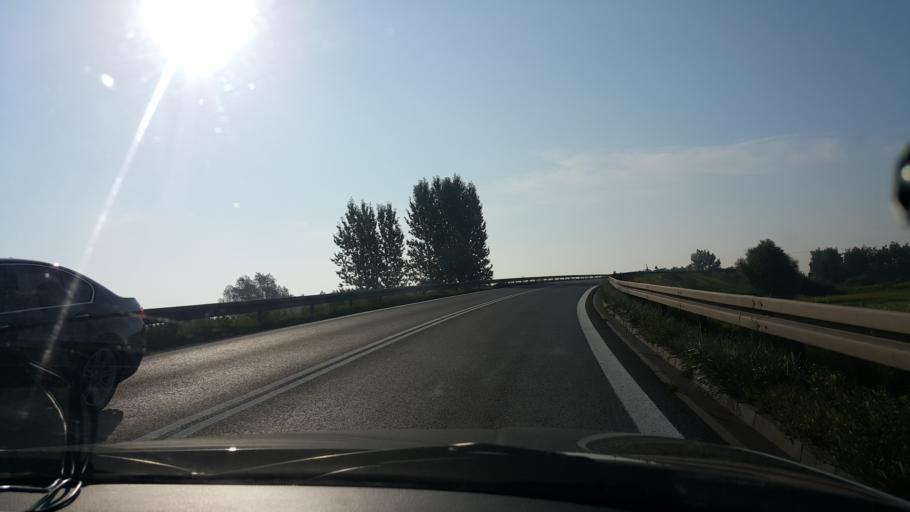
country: PL
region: Masovian Voivodeship
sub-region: Powiat radomski
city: Jastrzebia
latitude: 51.4129
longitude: 21.2347
